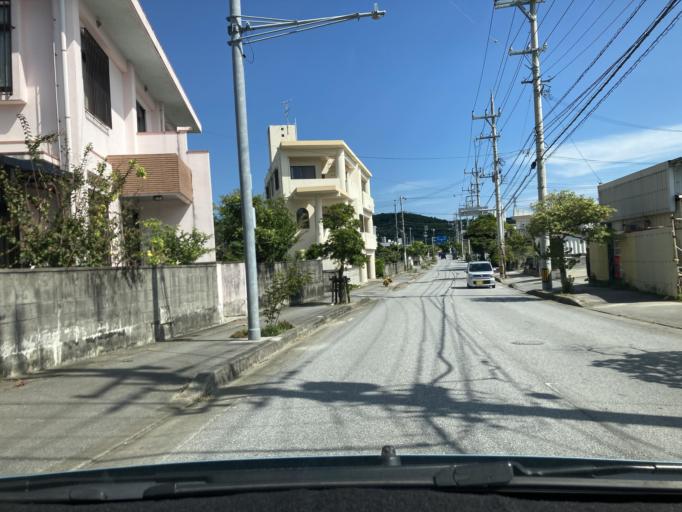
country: JP
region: Okinawa
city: Ginowan
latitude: 26.2293
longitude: 127.7517
